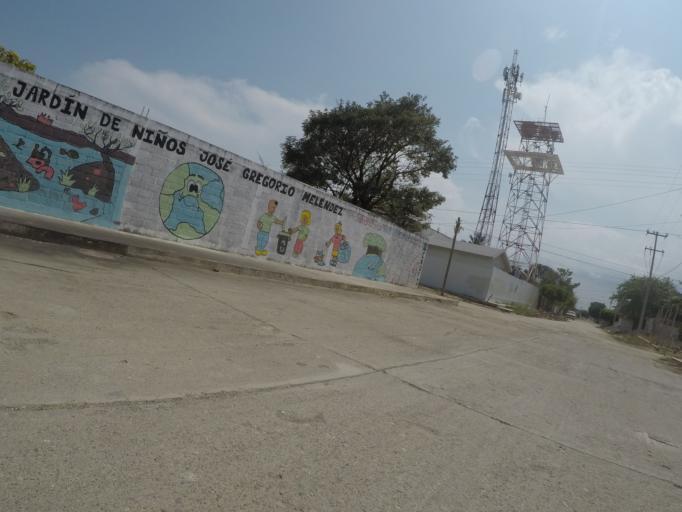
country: MX
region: Oaxaca
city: Union Hidalgo
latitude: 16.4735
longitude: -94.8306
